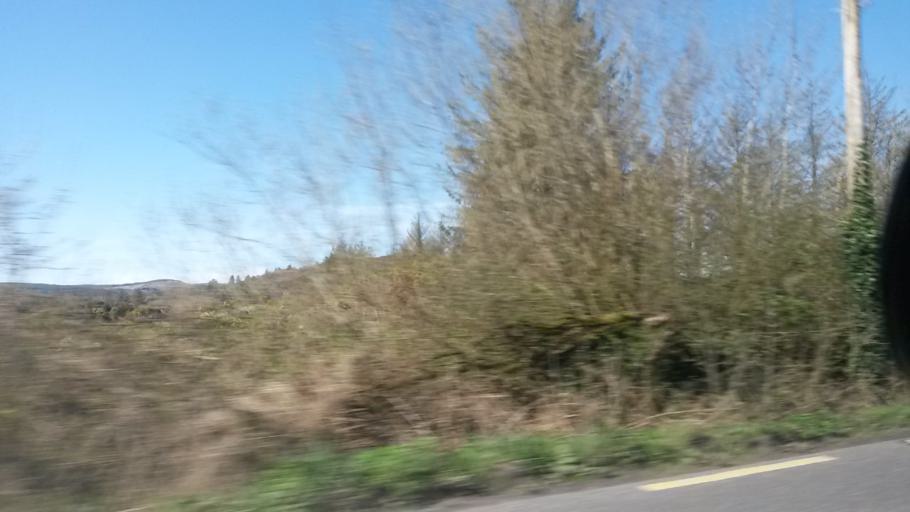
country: IE
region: Munster
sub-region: County Cork
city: Millstreet
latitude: 51.9312
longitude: -9.1260
